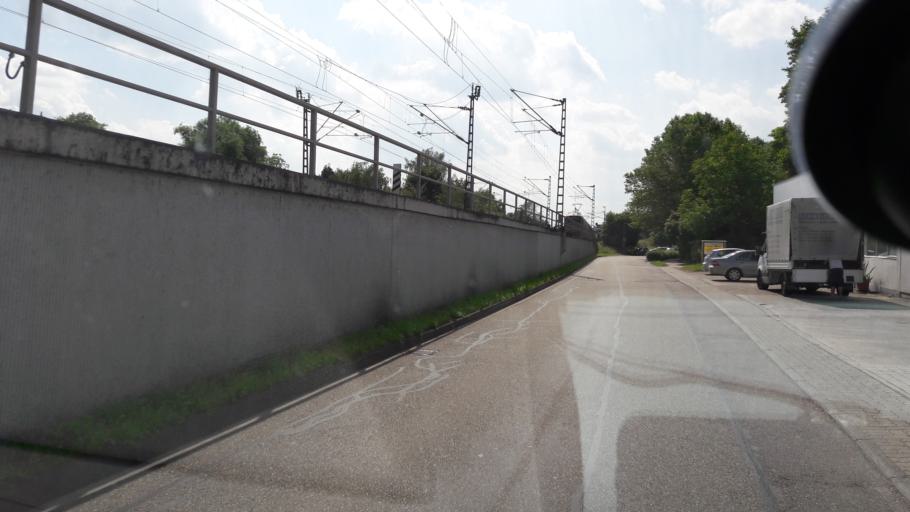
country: DE
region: Baden-Wuerttemberg
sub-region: Karlsruhe Region
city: Weingarten
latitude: 49.0067
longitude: 8.5233
